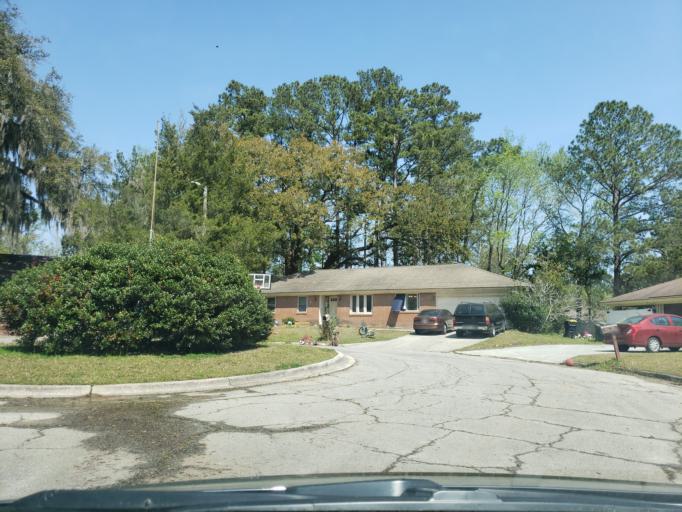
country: US
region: Georgia
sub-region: Chatham County
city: Montgomery
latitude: 31.9950
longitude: -81.1379
